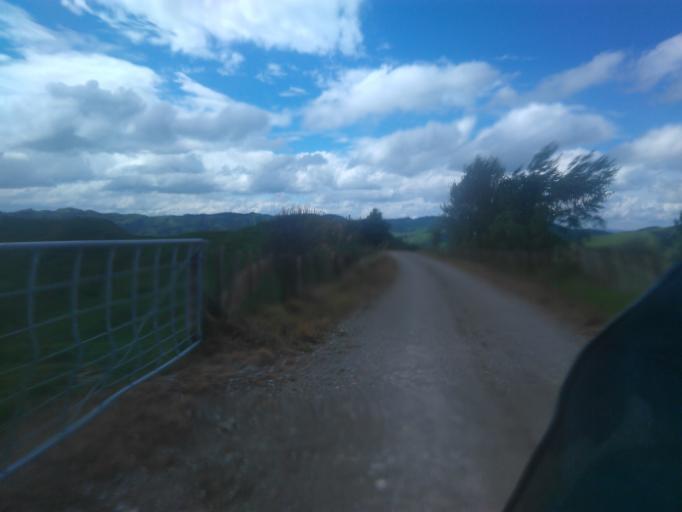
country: NZ
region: Gisborne
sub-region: Gisborne District
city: Gisborne
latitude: -38.7669
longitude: 177.6405
